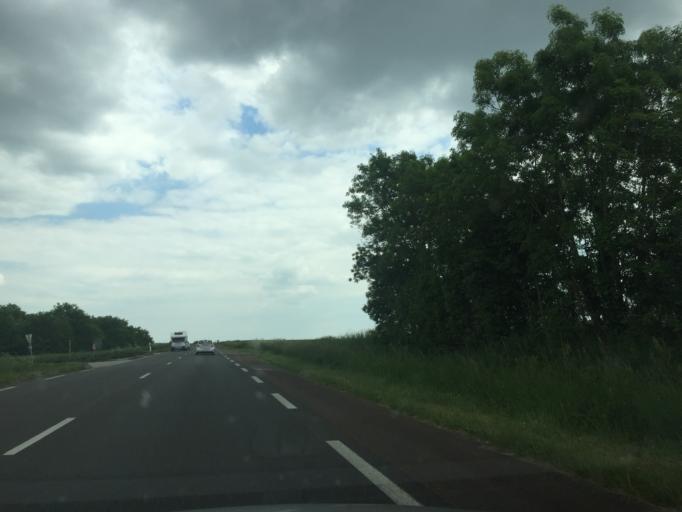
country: FR
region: Pays de la Loire
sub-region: Departement de la Vendee
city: Benet
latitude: 46.3825
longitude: -0.6118
